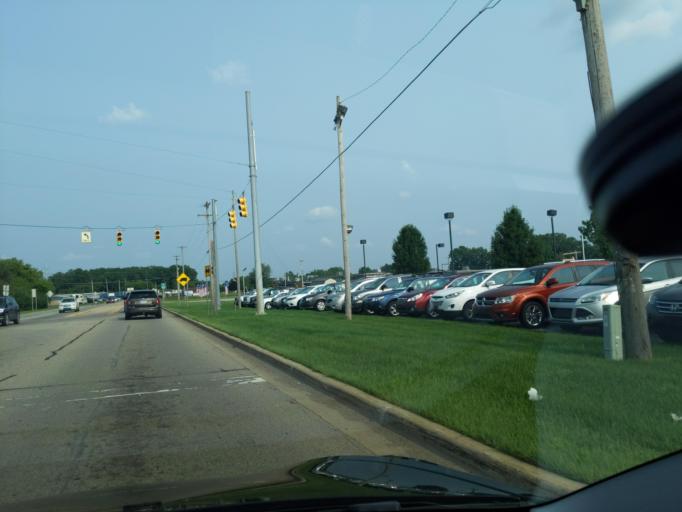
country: US
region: Michigan
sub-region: Jackson County
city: Jackson
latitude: 42.2513
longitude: -84.4481
